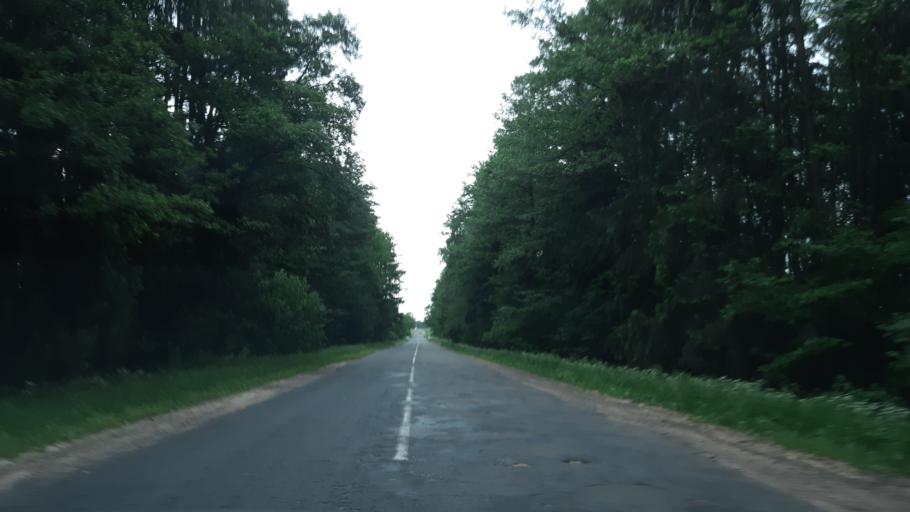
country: BY
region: Minsk
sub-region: Smalyavitski Rayon
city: Oktjabr'skij
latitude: 54.1112
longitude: 28.1689
